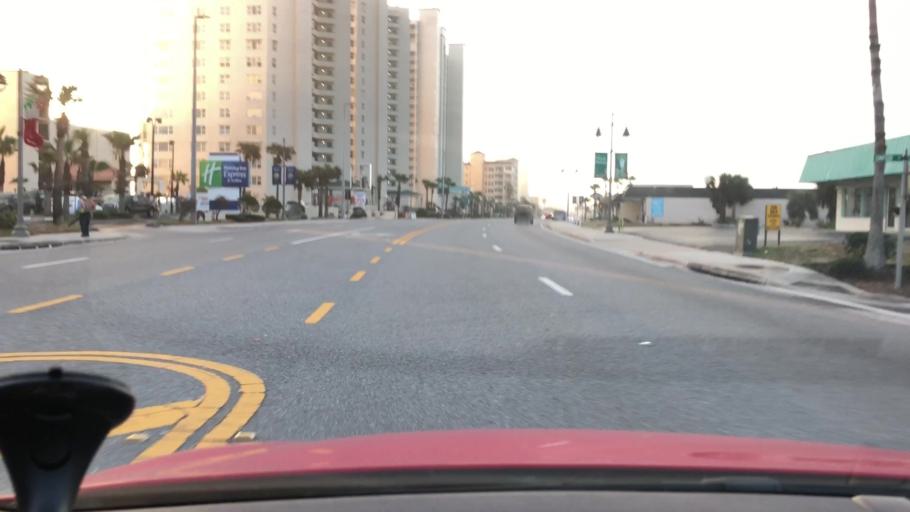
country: US
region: Florida
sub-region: Volusia County
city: Daytona Beach Shores
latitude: 29.1565
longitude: -80.9722
